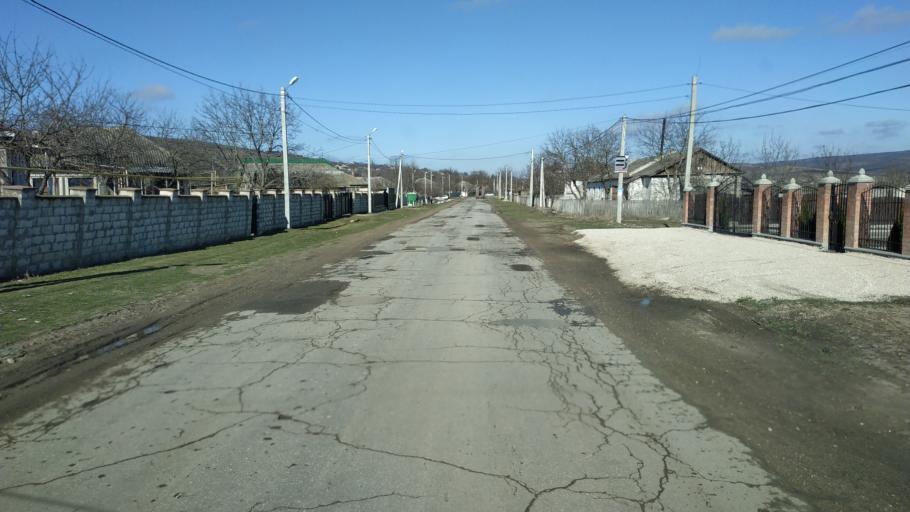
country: MD
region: Hincesti
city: Hincesti
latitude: 46.9537
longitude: 28.6089
